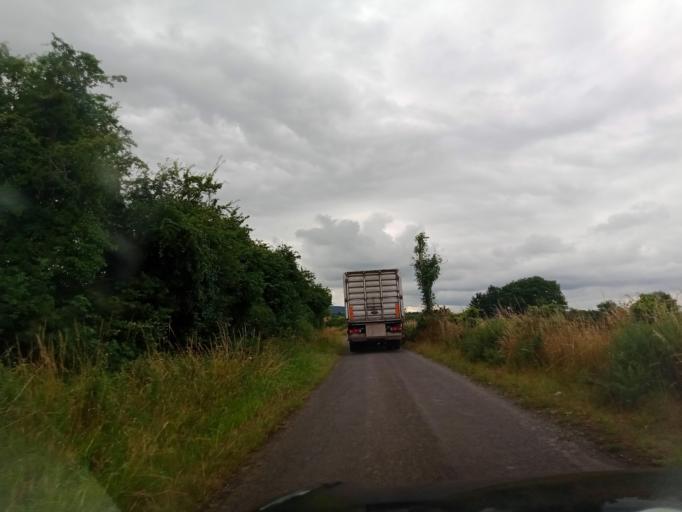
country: IE
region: Leinster
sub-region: Laois
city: Stradbally
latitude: 52.9644
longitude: -7.1615
